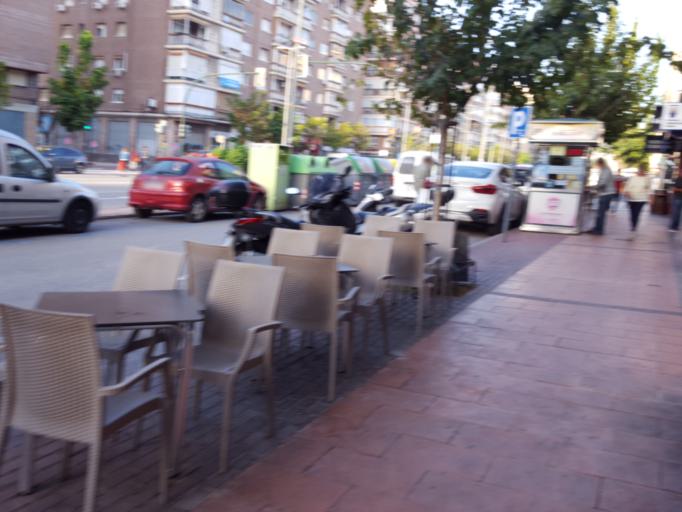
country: ES
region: Murcia
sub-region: Murcia
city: Murcia
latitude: 37.9919
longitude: -1.1368
